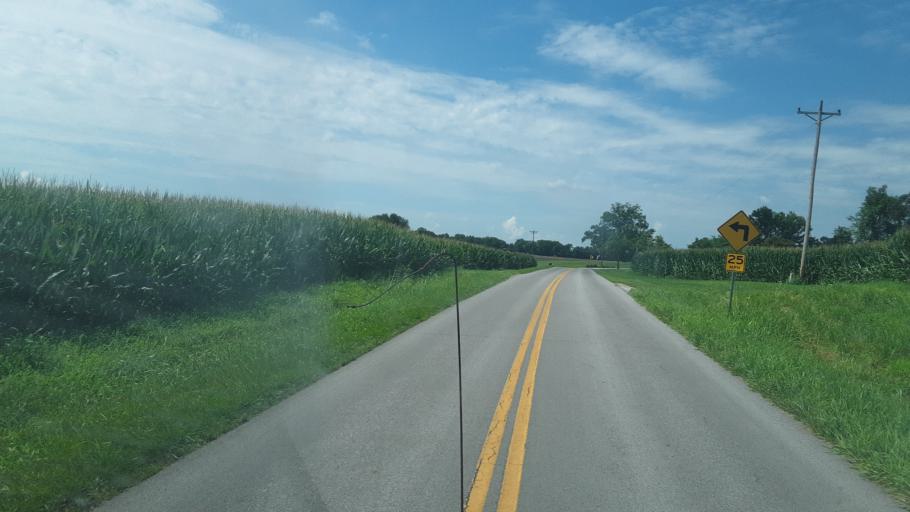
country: US
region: Kentucky
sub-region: Christian County
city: Oak Grove
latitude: 36.7520
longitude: -87.3178
